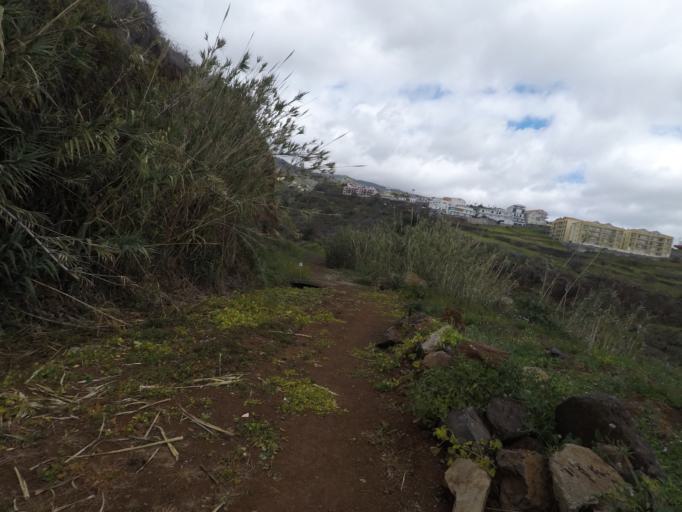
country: PT
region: Madeira
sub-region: Calheta
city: Estreito da Calheta
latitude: 32.7296
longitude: -17.1821
